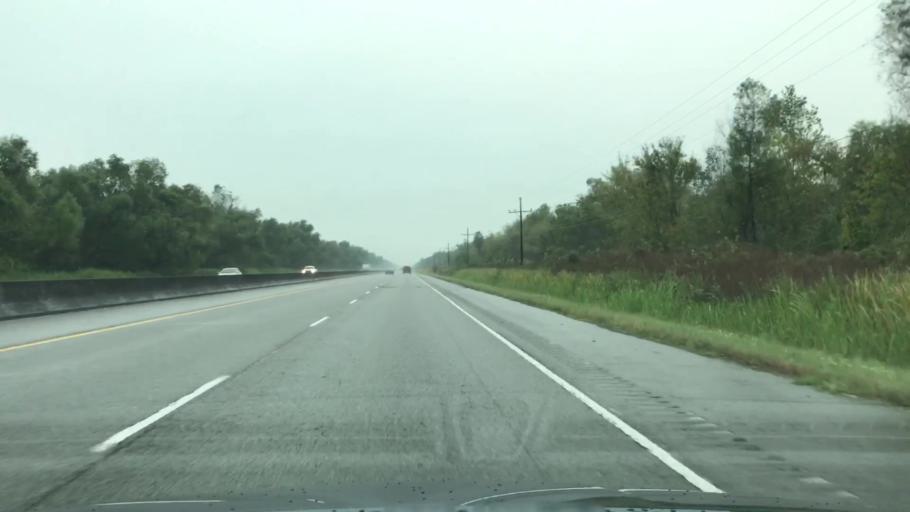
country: US
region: Louisiana
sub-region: Saint Charles Parish
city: Des Allemands
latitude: 29.7818
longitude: -90.5244
